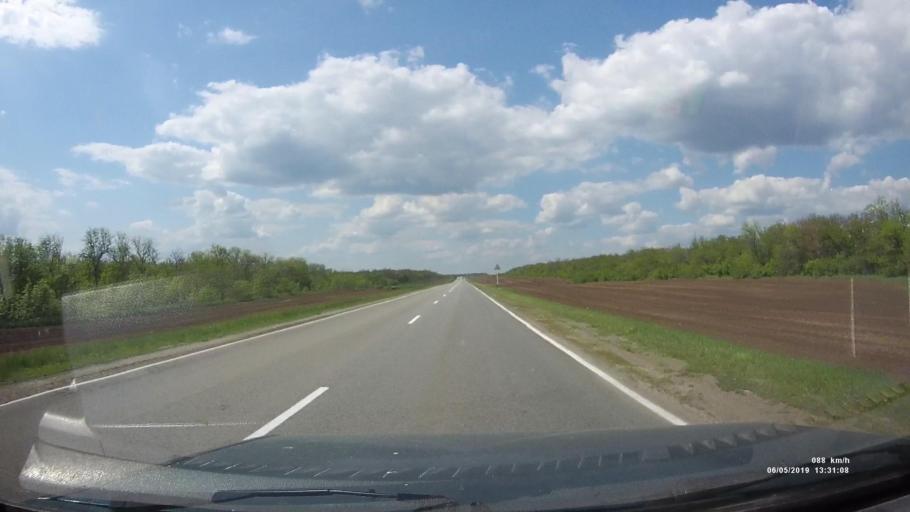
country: RU
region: Rostov
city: Ust'-Donetskiy
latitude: 47.6744
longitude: 40.8154
